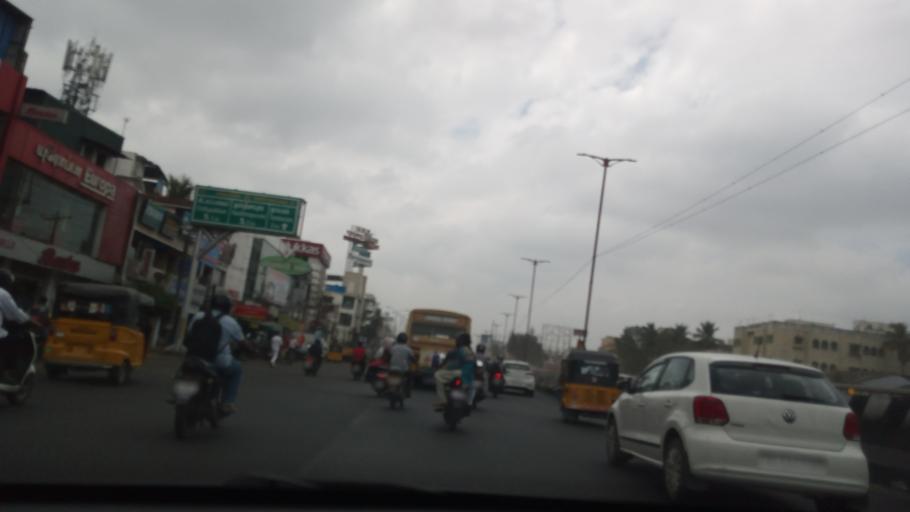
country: IN
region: Tamil Nadu
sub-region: Kancheepuram
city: Pallavaram
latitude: 12.9501
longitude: 80.1393
